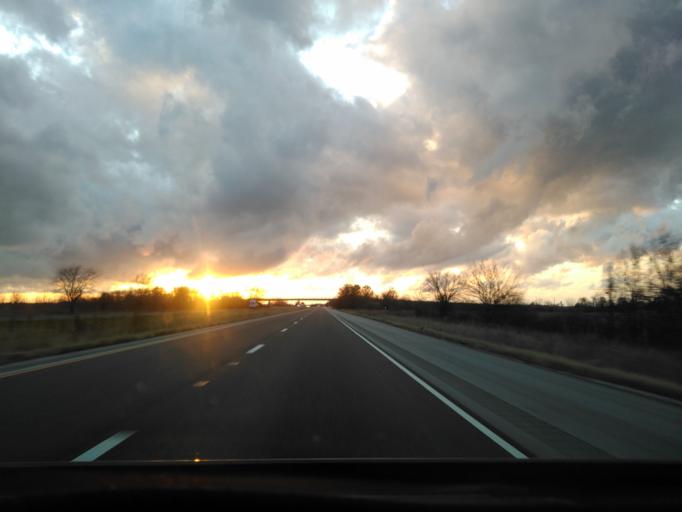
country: US
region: Illinois
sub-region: Fayette County
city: Saint Elmo
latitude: 38.9982
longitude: -88.9042
